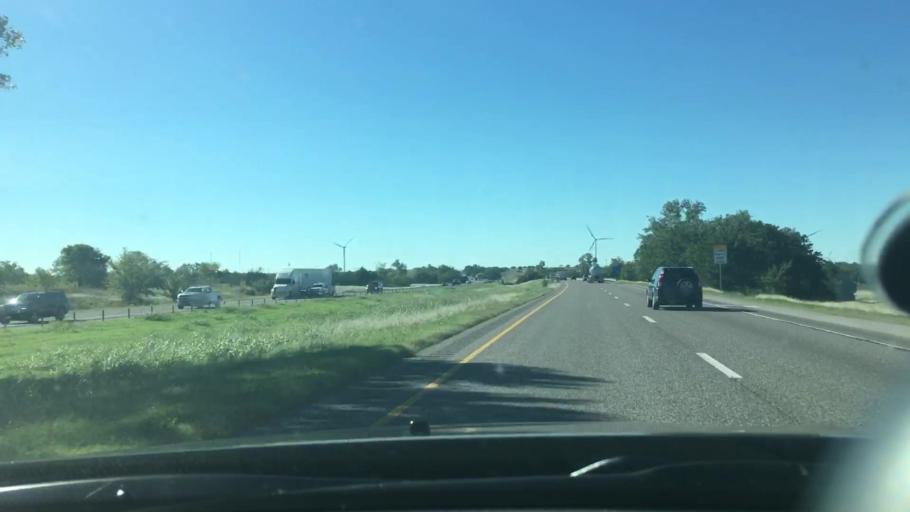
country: US
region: Oklahoma
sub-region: Murray County
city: Davis
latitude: 34.4029
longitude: -97.1409
